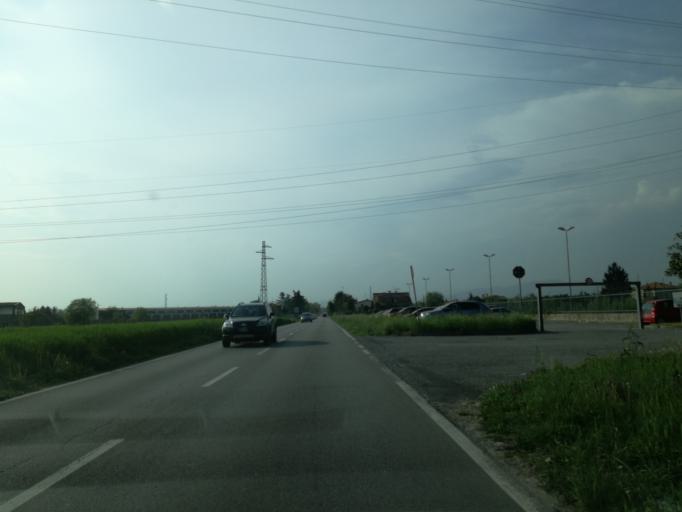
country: IT
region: Lombardy
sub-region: Provincia di Lecco
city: Verderio Superiore
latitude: 45.6594
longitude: 9.4535
